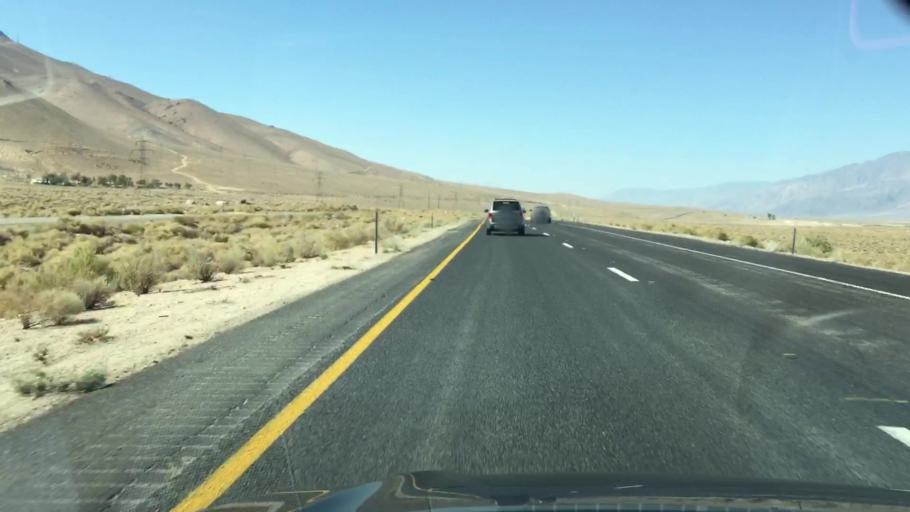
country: US
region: California
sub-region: Inyo County
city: Lone Pine
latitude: 36.4331
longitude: -118.0320
